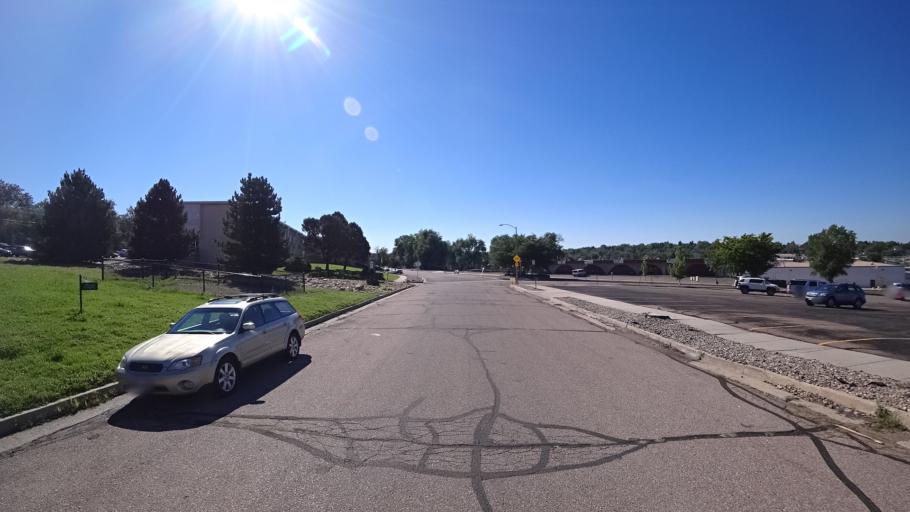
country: US
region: Colorado
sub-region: El Paso County
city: Colorado Springs
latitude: 38.8605
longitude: -104.7930
